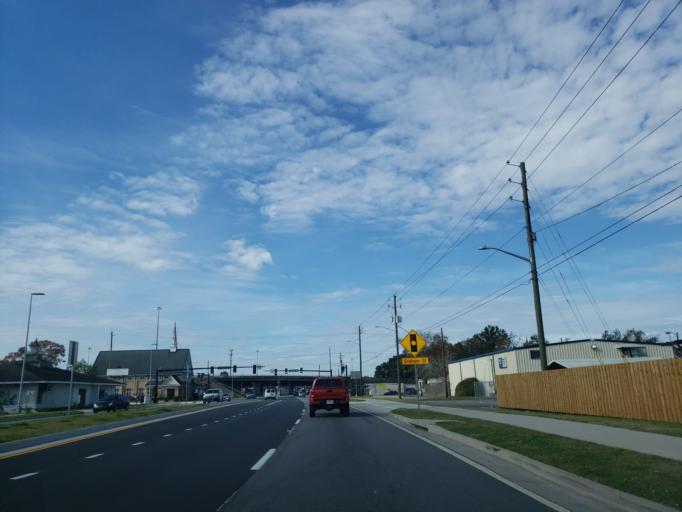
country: US
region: Georgia
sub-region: Chatham County
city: Savannah
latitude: 32.0901
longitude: -81.1246
